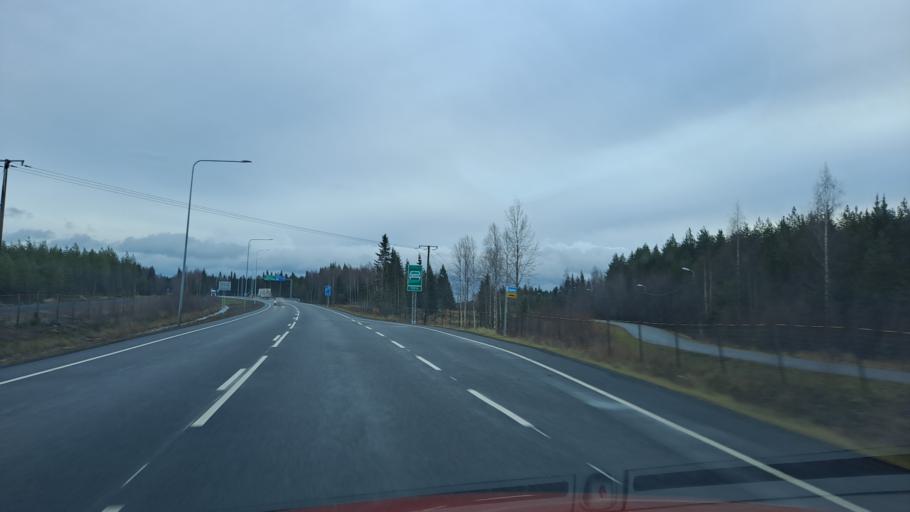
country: FI
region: Northern Ostrobothnia
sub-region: Oulunkaari
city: Ii
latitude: 65.2689
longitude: 25.3626
